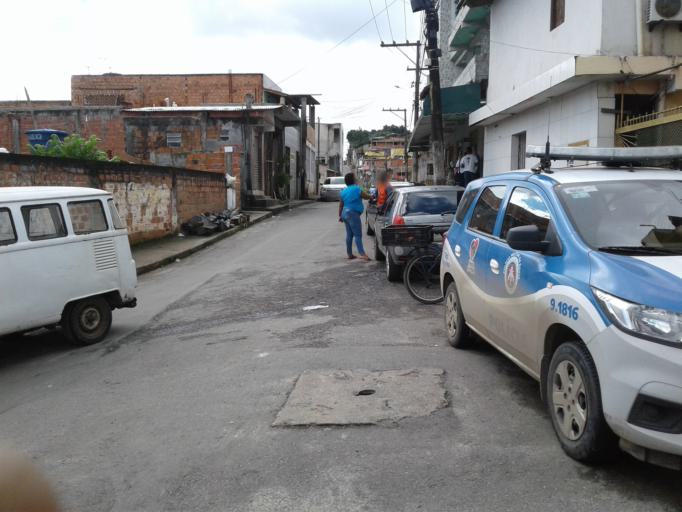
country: BR
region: Bahia
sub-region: Salvador
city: Salvador
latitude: -12.8839
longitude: -38.4751
